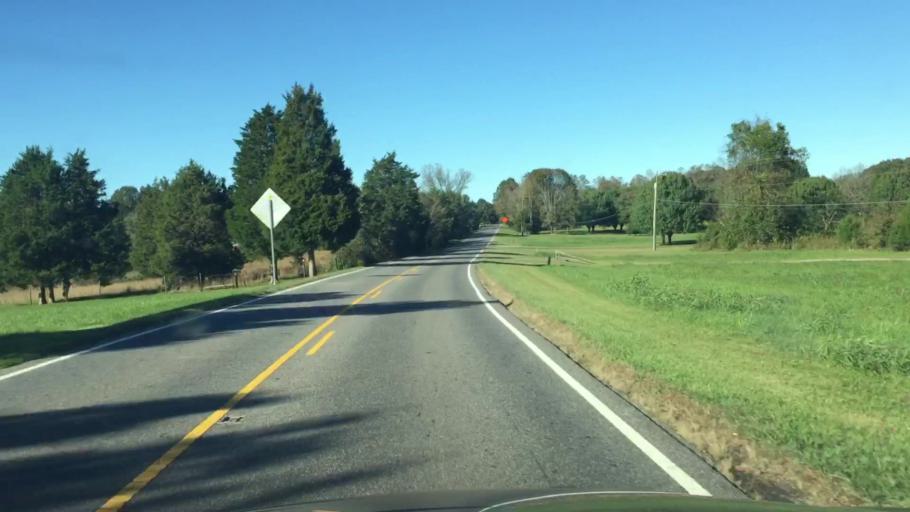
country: US
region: North Carolina
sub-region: Gaston County
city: Davidson
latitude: 35.5202
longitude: -80.7705
